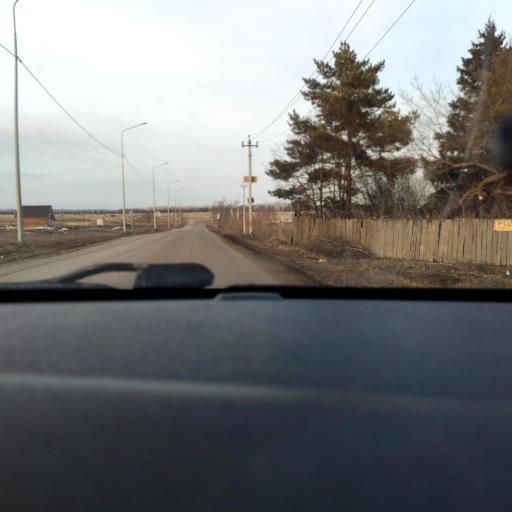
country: RU
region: Bashkortostan
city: Avdon
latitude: 54.5554
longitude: 55.7606
